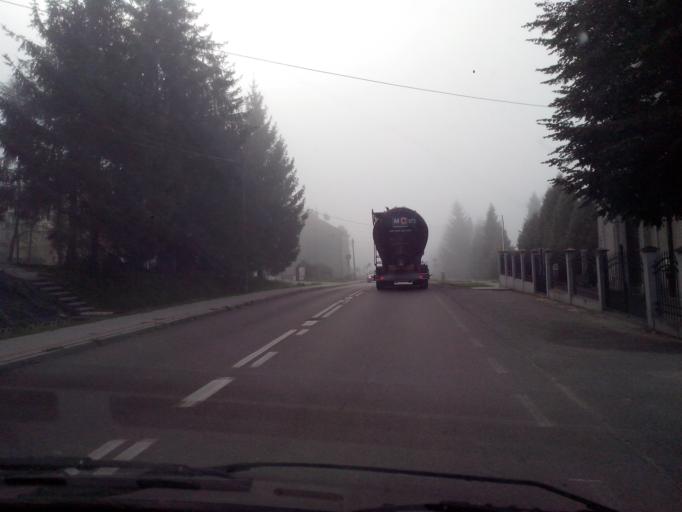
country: PL
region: Subcarpathian Voivodeship
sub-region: Przemysl
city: Przemysl
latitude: 49.7998
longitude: 22.7131
